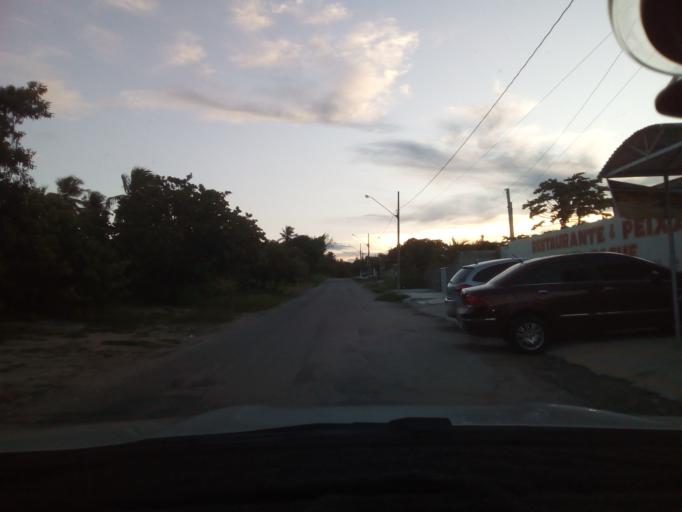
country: BR
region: Paraiba
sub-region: Joao Pessoa
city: Joao Pessoa
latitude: -7.2002
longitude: -34.8005
